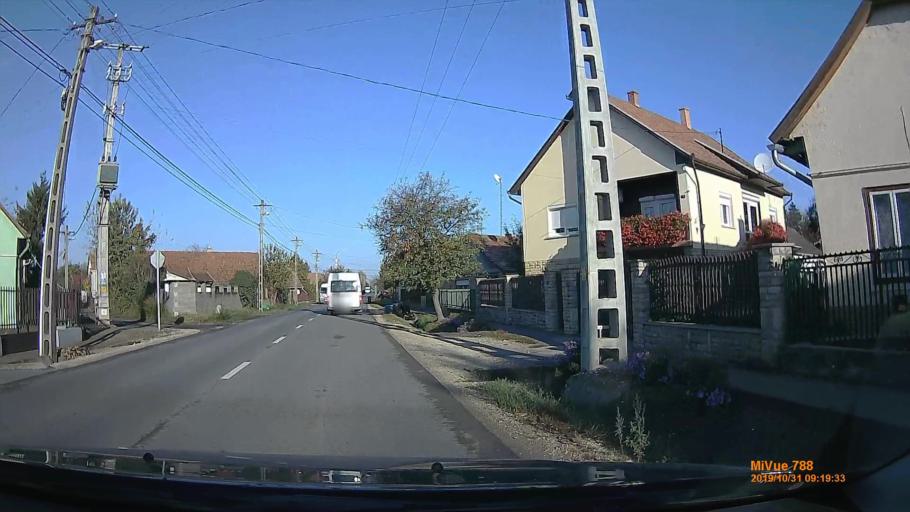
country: HU
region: Pest
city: Gyomro
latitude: 47.4182
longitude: 19.3907
